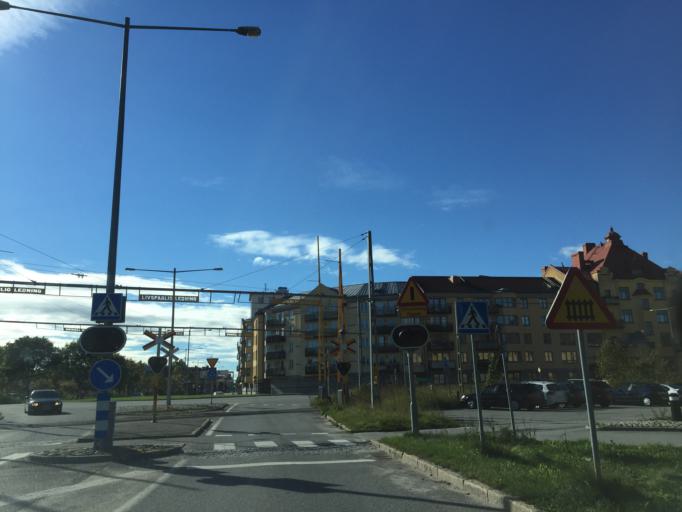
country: SE
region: OErebro
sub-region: Orebro Kommun
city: Orebro
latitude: 59.2779
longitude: 15.2233
